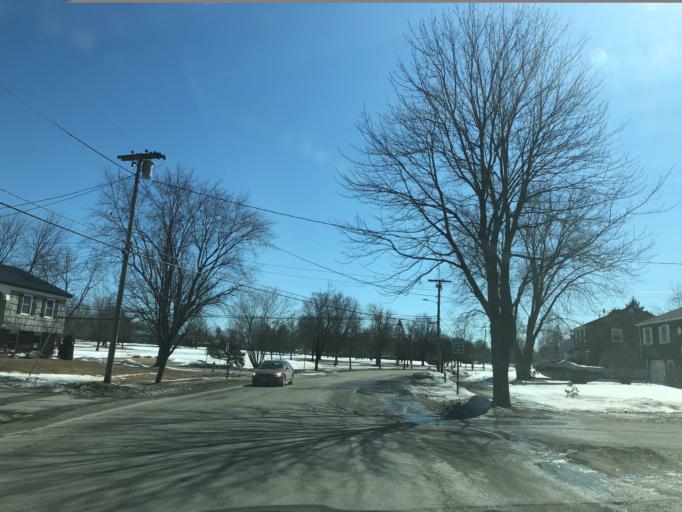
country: US
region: Maine
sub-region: Penobscot County
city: Brewer
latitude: 44.8208
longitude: -68.7600
